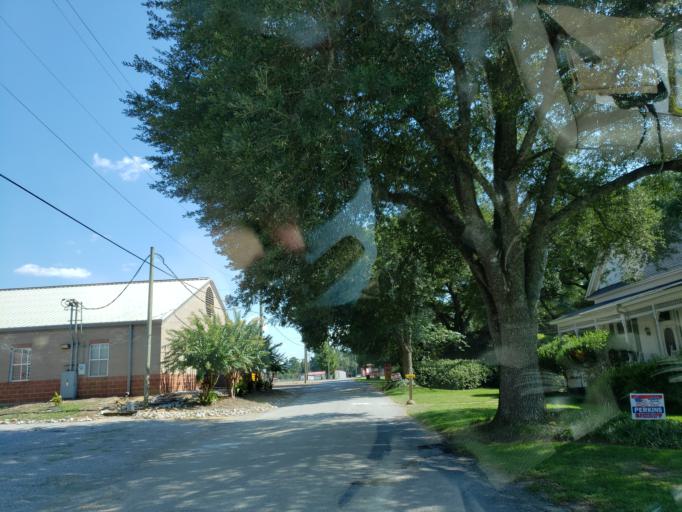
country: US
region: Mississippi
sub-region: Covington County
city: Collins
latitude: 31.5608
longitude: -89.5004
